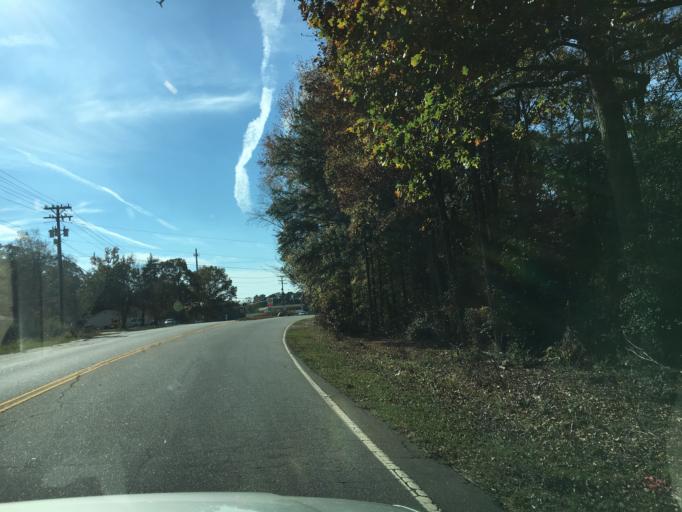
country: US
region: South Carolina
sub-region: Anderson County
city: Anderson
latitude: 34.5069
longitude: -82.6041
